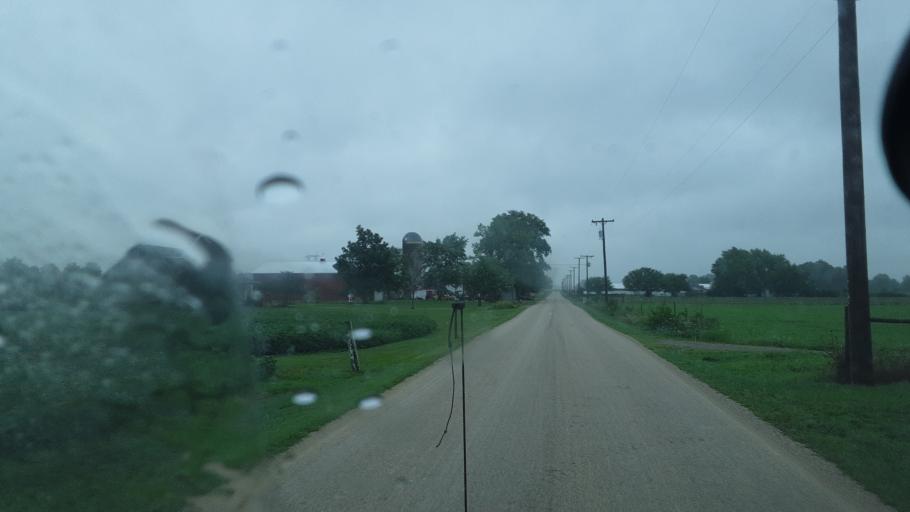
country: US
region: Indiana
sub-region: Adams County
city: Berne
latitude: 40.6871
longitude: -84.9460
